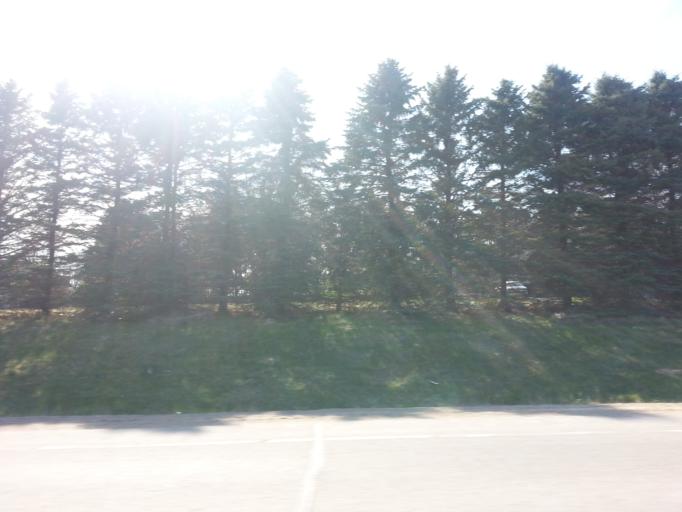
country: US
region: Wisconsin
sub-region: Pierce County
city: Ellsworth
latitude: 44.7525
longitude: -92.4871
